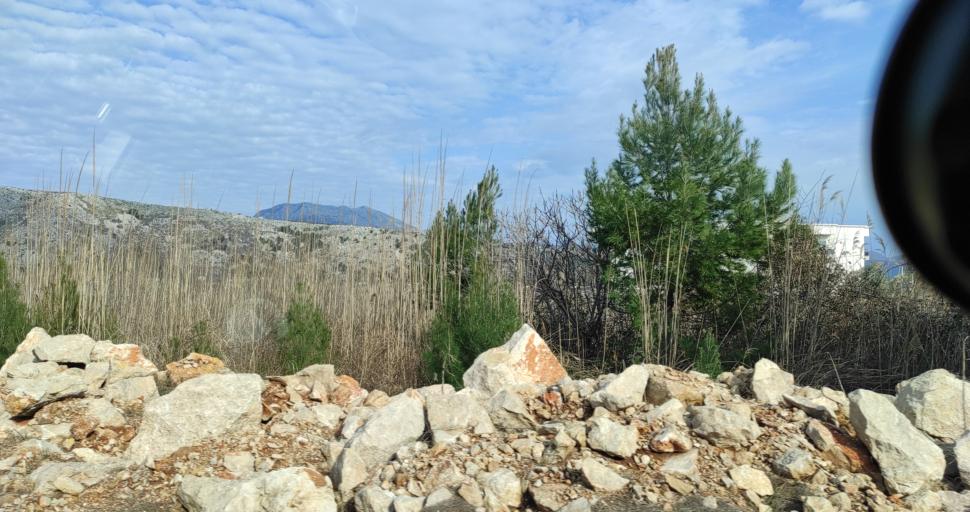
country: AL
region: Lezhe
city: Shengjin
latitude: 41.7910
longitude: 19.6031
